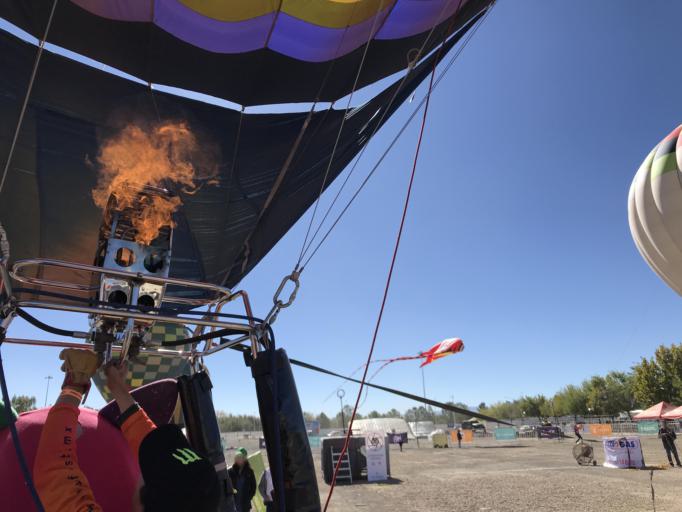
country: MX
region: Durango
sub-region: Durango
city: Sebastian Lerdo de Tejada
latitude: 23.9915
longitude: -104.6078
